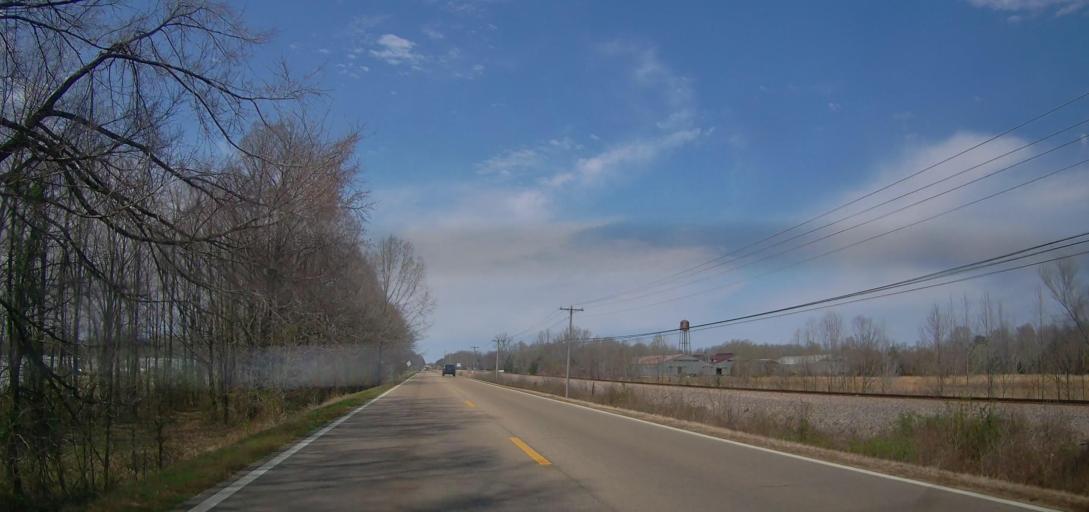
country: US
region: Mississippi
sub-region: Union County
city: New Albany
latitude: 34.5194
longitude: -89.0529
